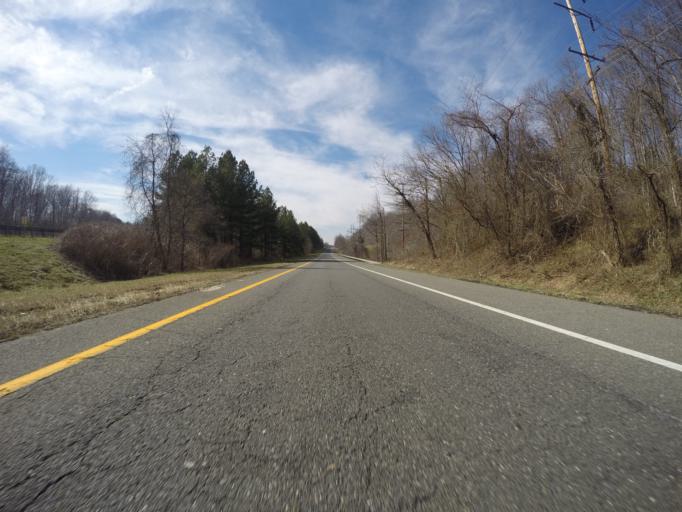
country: US
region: Maryland
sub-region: Anne Arundel County
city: Crownsville
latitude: 39.0430
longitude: -76.6107
